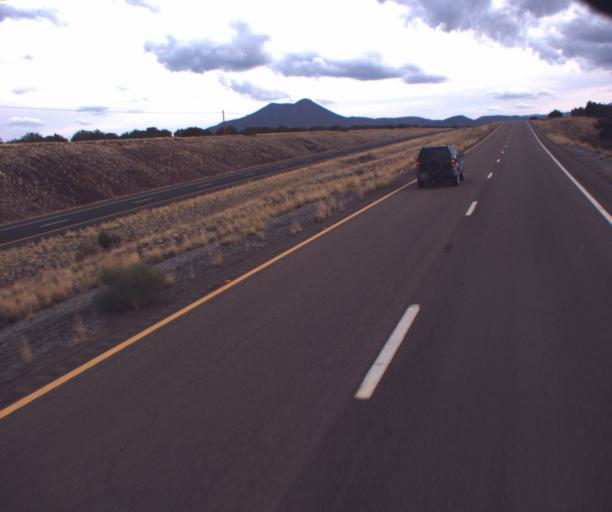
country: US
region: Arizona
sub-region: Coconino County
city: Flagstaff
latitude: 35.4911
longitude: -111.5551
